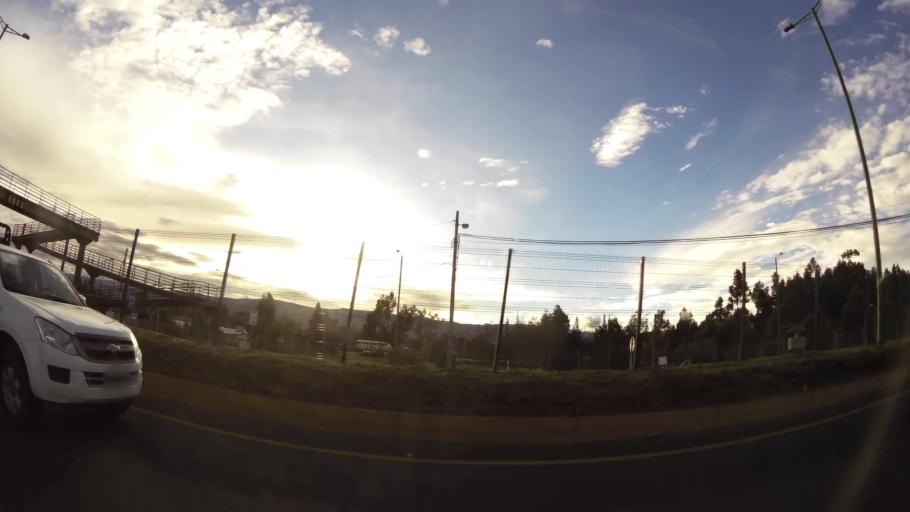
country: EC
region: Cotopaxi
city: Saquisili
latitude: -0.8510
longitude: -78.6195
